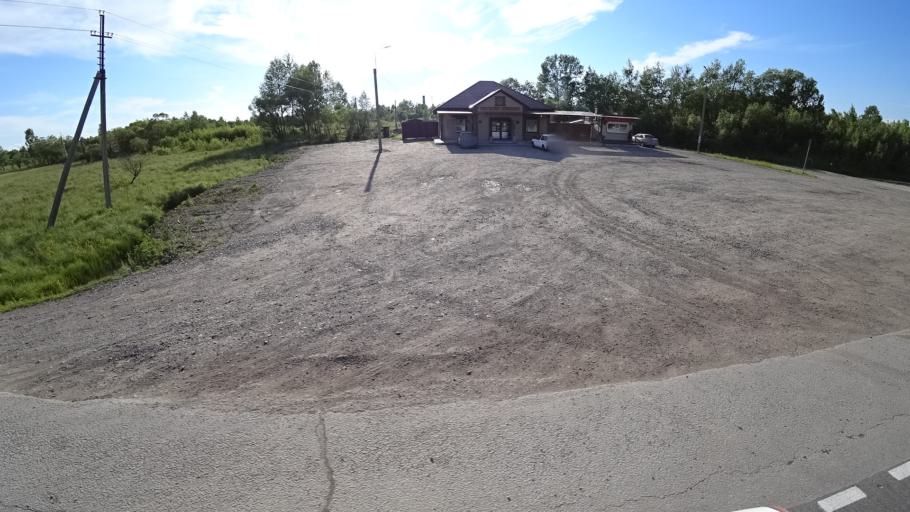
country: RU
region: Khabarovsk Krai
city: Khor
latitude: 47.8504
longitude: 134.9600
